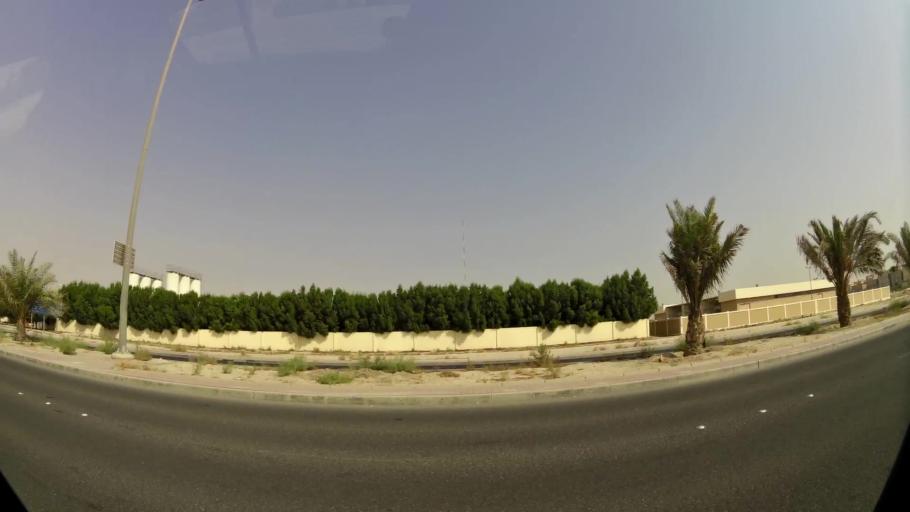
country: KW
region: Muhafazat al Jahra'
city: Al Jahra'
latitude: 29.3230
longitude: 47.7300
